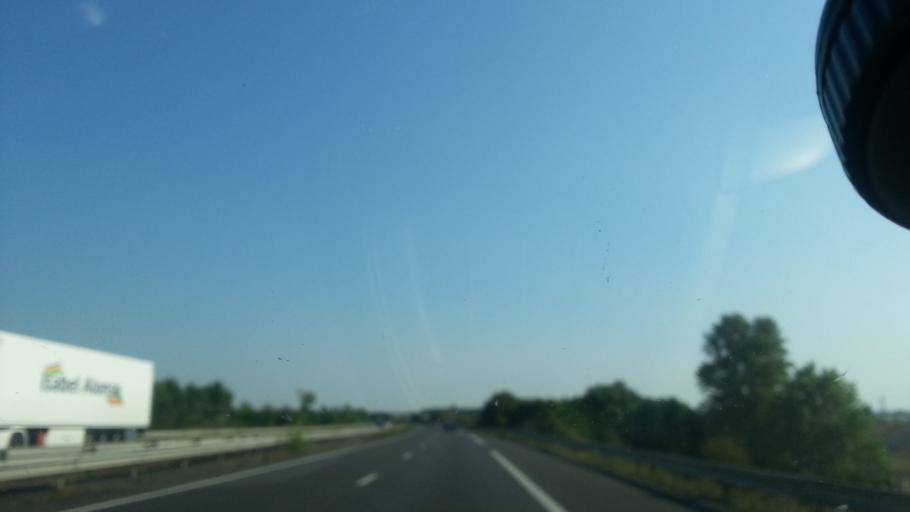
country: FR
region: Centre
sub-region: Departement d'Indre-et-Loire
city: La Celle-Saint-Avant
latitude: 47.0454
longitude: 0.5845
